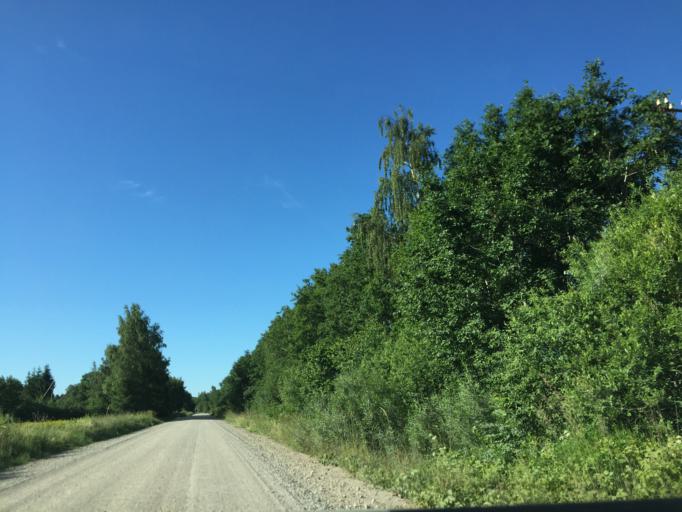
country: LV
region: Ventspils Rajons
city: Piltene
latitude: 57.3207
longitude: 21.6892
